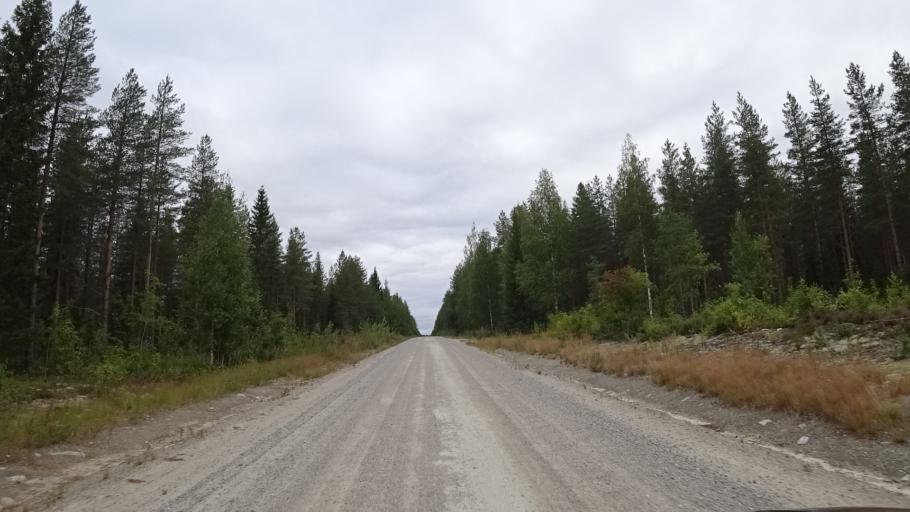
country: FI
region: North Karelia
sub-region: Joensuu
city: Eno
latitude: 63.1546
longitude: 30.6097
